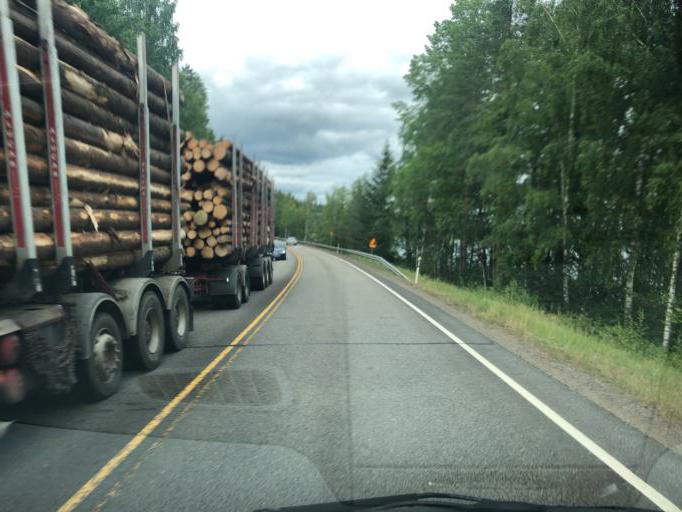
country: FI
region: Kymenlaakso
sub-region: Kouvola
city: Kouvola
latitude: 60.9574
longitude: 26.8624
